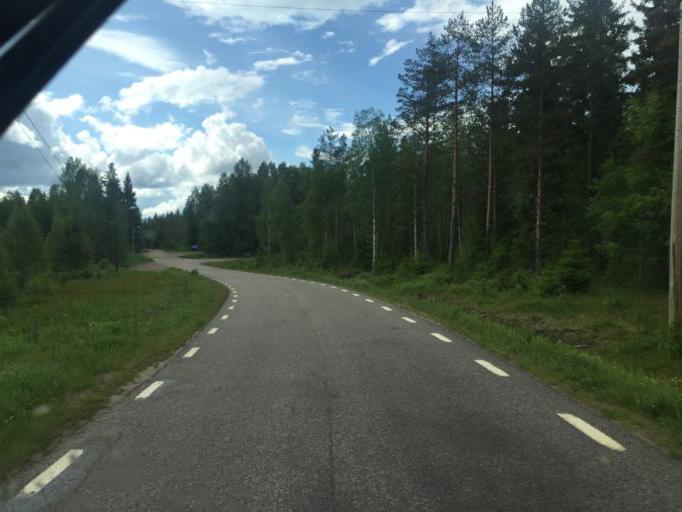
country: SE
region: Vaermland
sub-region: Hagfors Kommun
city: Hagfors
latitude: 60.2904
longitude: 13.8639
